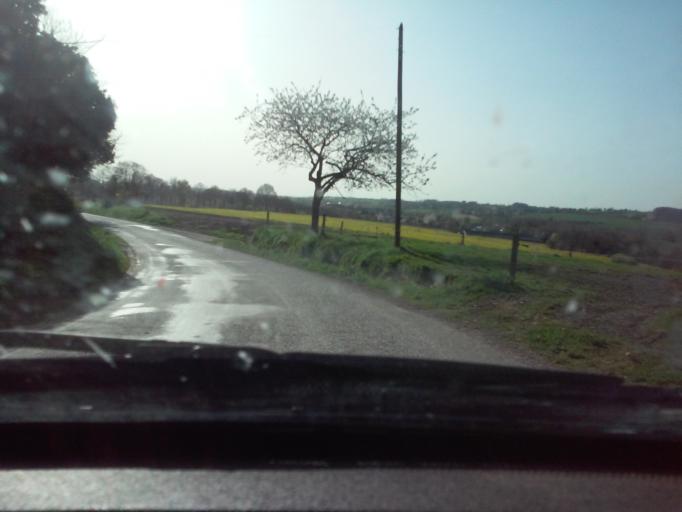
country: FR
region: Brittany
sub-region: Departement d'Ille-et-Vilaine
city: Romagne
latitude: 48.2976
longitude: -1.2971
